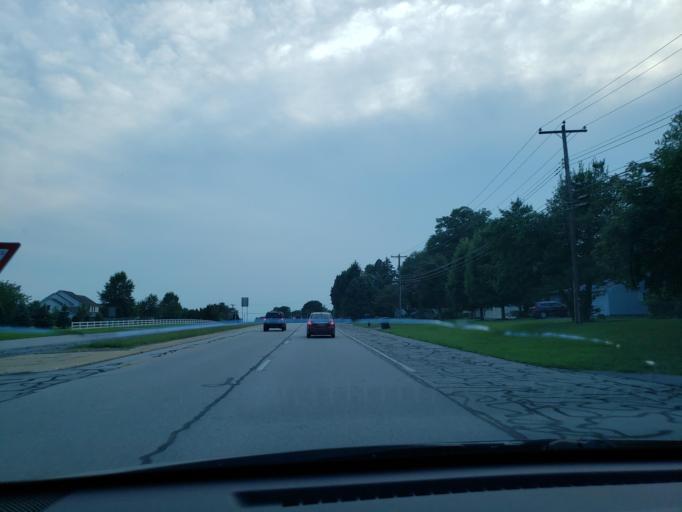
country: US
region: Delaware
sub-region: Kent County
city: Highland Acres
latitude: 39.1175
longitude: -75.5187
